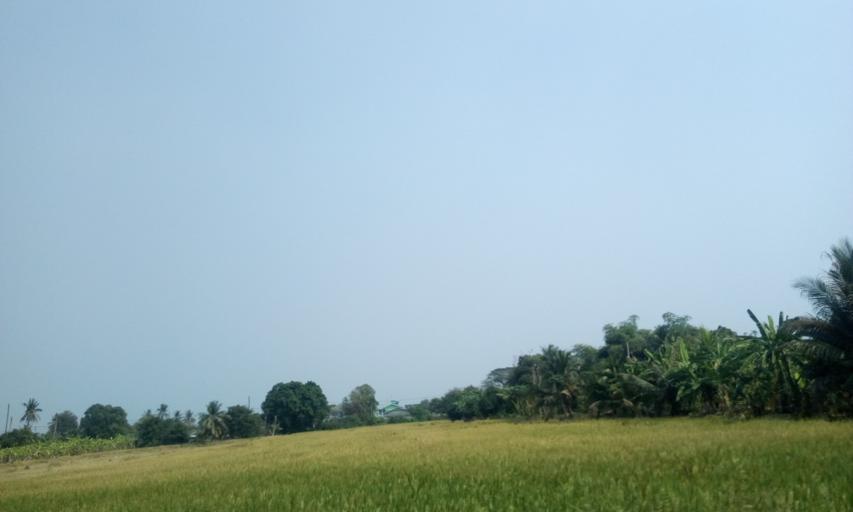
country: TH
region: Pathum Thani
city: Lam Luk Ka
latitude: 13.9456
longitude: 100.7245
